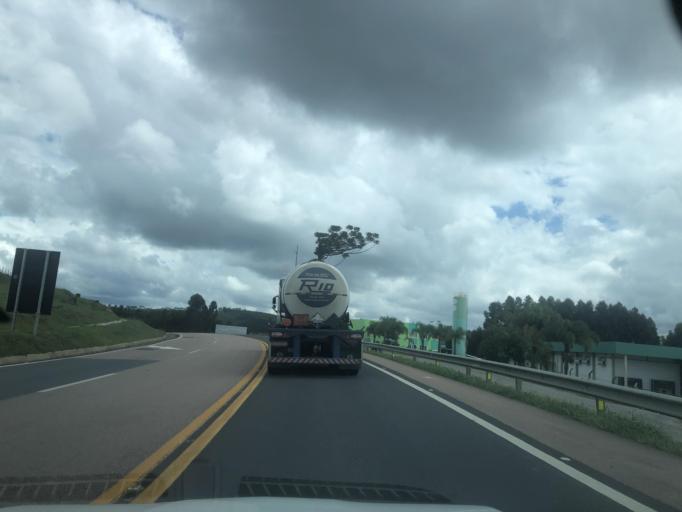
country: BR
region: Parana
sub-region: Rio Negro
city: Rio Negro
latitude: -26.0623
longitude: -49.7315
